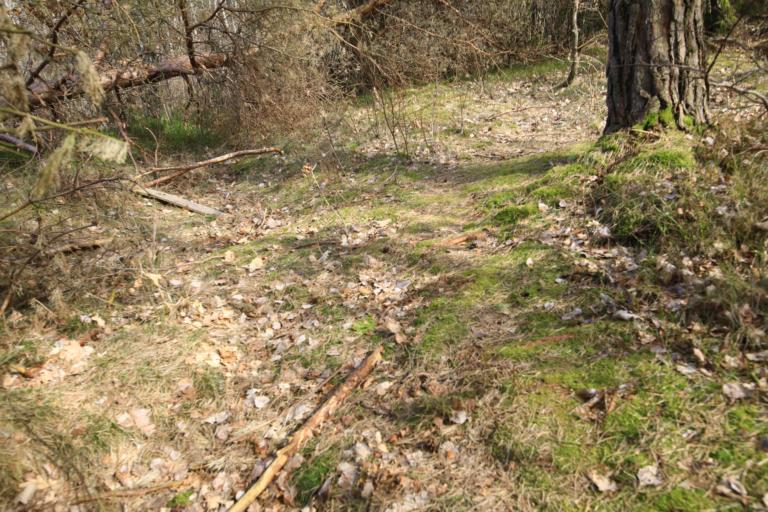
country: SE
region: Halland
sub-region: Varbergs Kommun
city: Varberg
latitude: 57.1385
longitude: 12.2873
